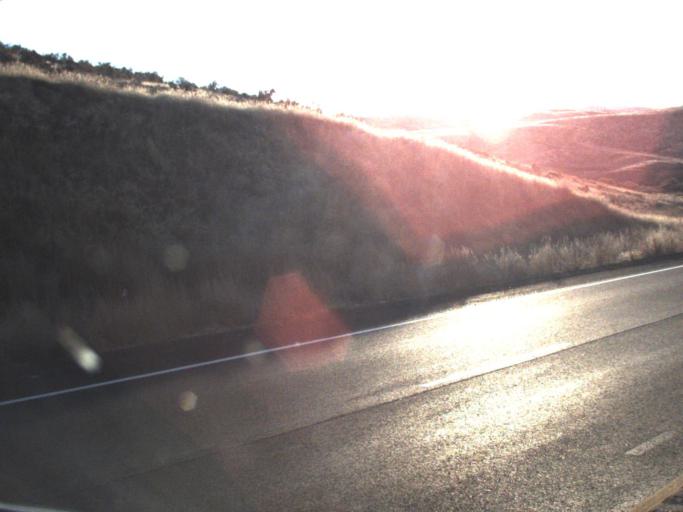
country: US
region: Washington
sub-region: Walla Walla County
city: Burbank
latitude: 46.0713
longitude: -118.7772
